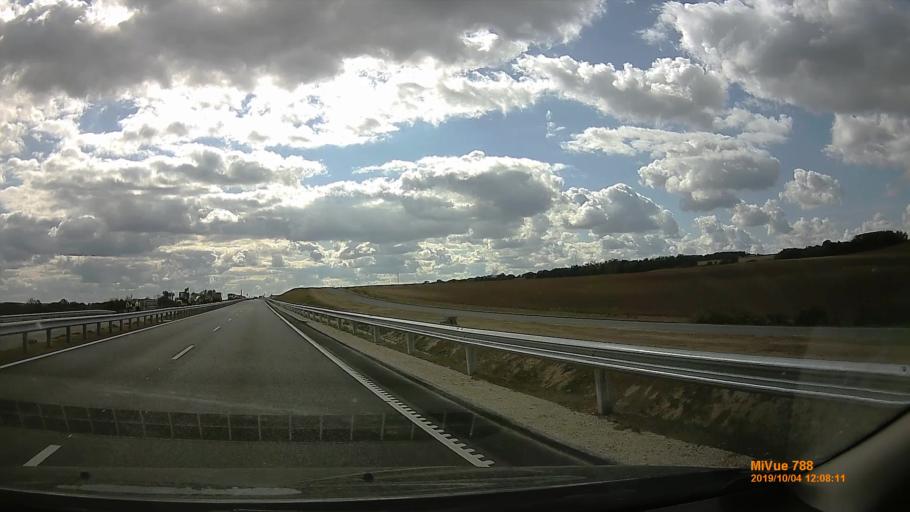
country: HU
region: Somogy
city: Karad
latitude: 46.5308
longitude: 17.8174
